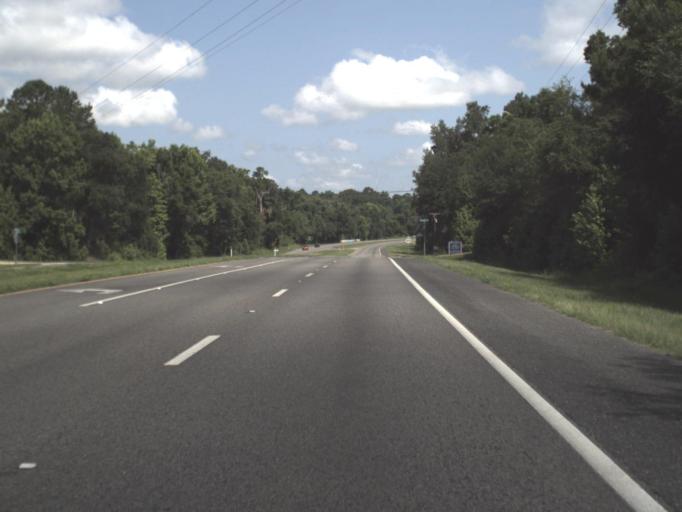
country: US
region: Florida
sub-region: Alachua County
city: Gainesville
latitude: 29.5217
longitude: -82.3018
